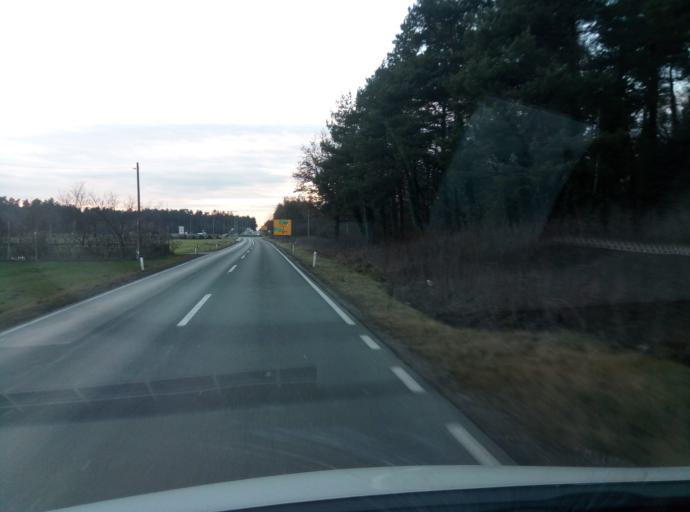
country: SI
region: Kidricevo
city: Kidricevo
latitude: 46.4126
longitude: 15.8166
